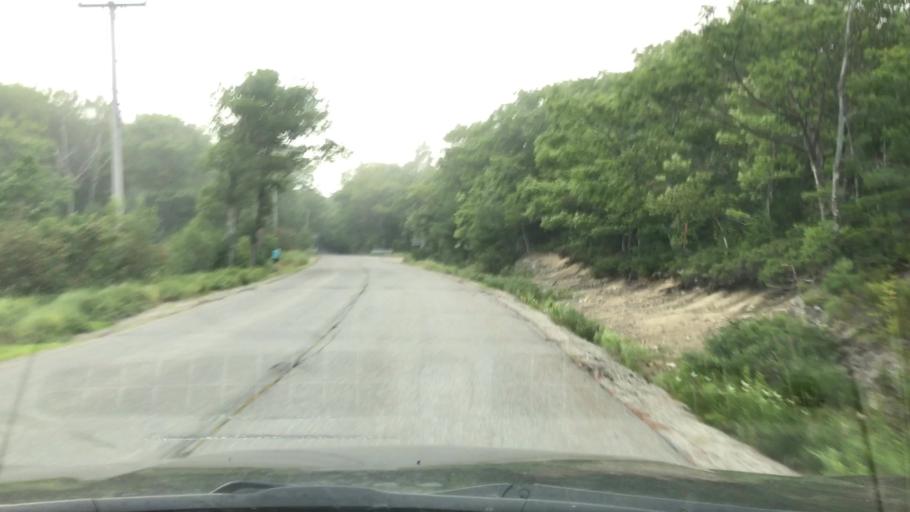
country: US
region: Maine
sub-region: Hancock County
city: Bar Harbor
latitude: 44.3549
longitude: -68.1846
